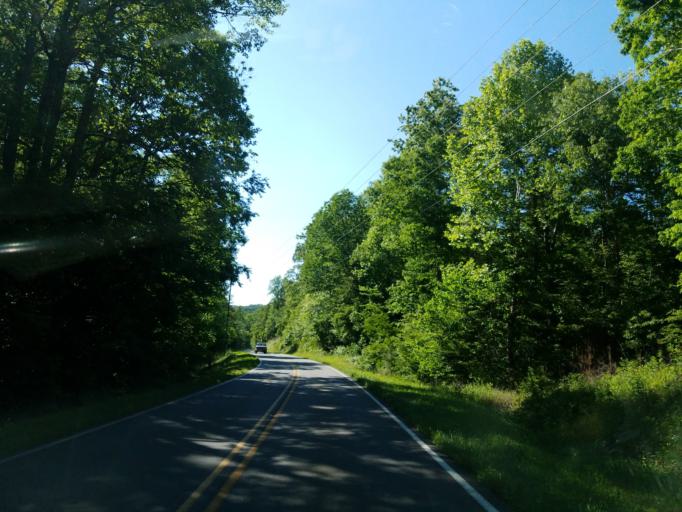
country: US
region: Georgia
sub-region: Pickens County
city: Jasper
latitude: 34.5193
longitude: -84.5054
